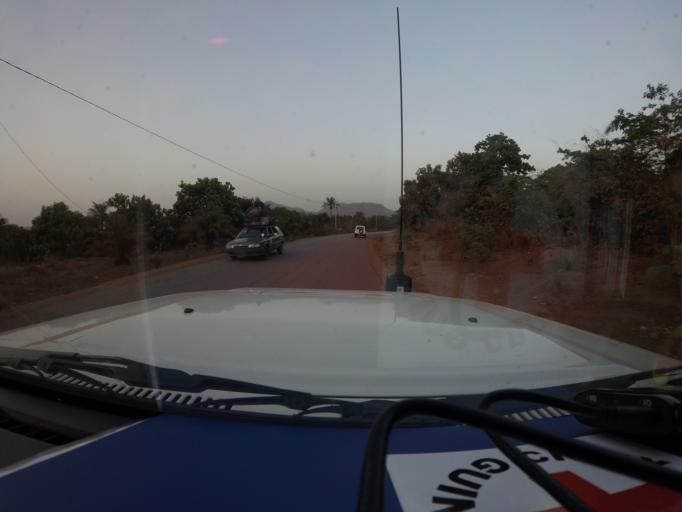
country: GN
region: Kindia
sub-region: Kindia
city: Kindia
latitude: 9.8525
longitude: -13.0886
